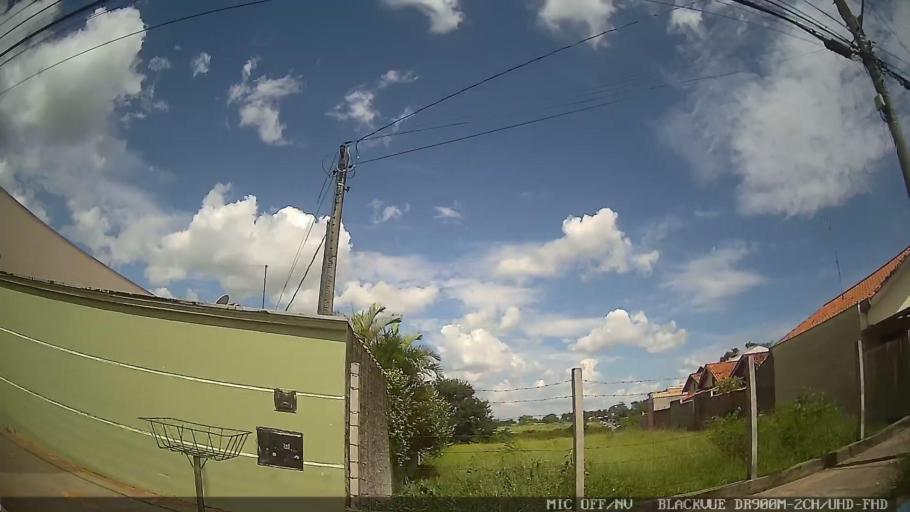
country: BR
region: Sao Paulo
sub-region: Conchas
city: Conchas
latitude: -23.0326
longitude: -48.0154
